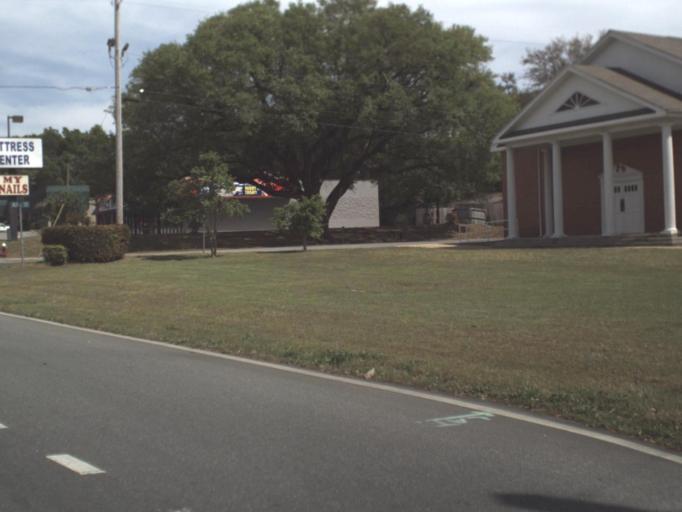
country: US
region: Florida
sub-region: Santa Rosa County
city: Pace
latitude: 30.6035
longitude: -87.1486
